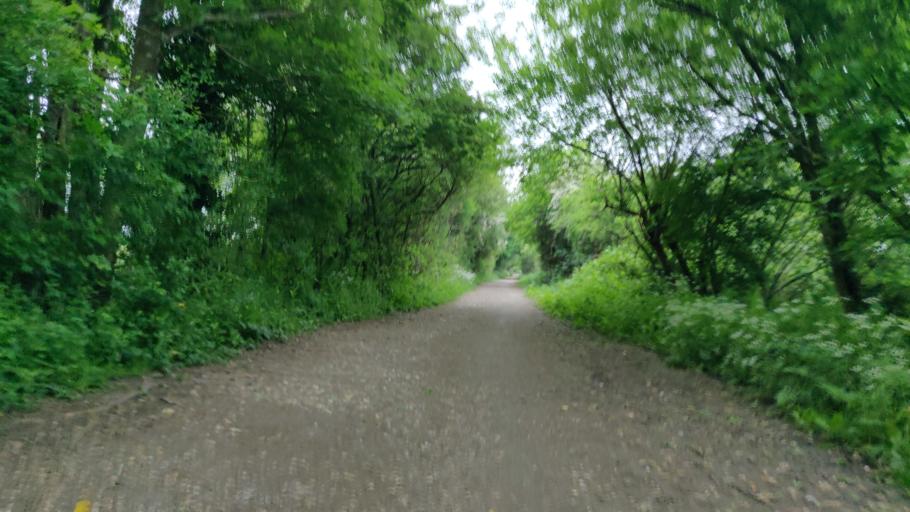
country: GB
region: England
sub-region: West Sussex
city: Southwater
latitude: 51.0009
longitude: -0.3208
